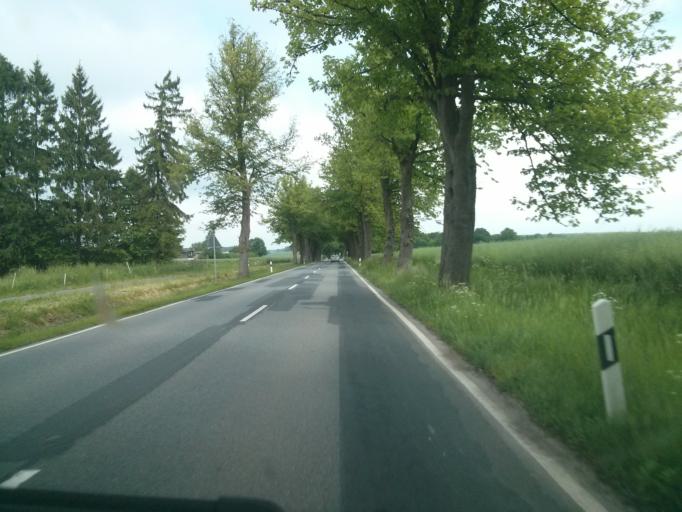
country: DE
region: Mecklenburg-Vorpommern
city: Tribsees
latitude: 54.1562
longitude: 12.8046
